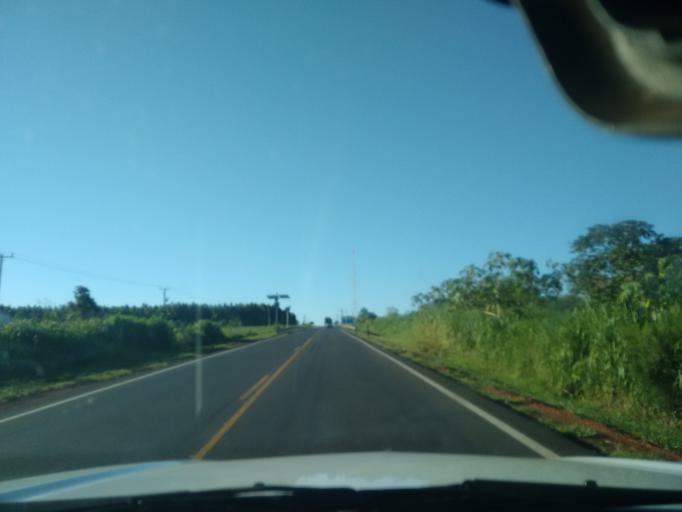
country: BR
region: Mato Grosso do Sul
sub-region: Eldorado
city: Eldorado
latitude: -23.8722
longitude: -54.3250
